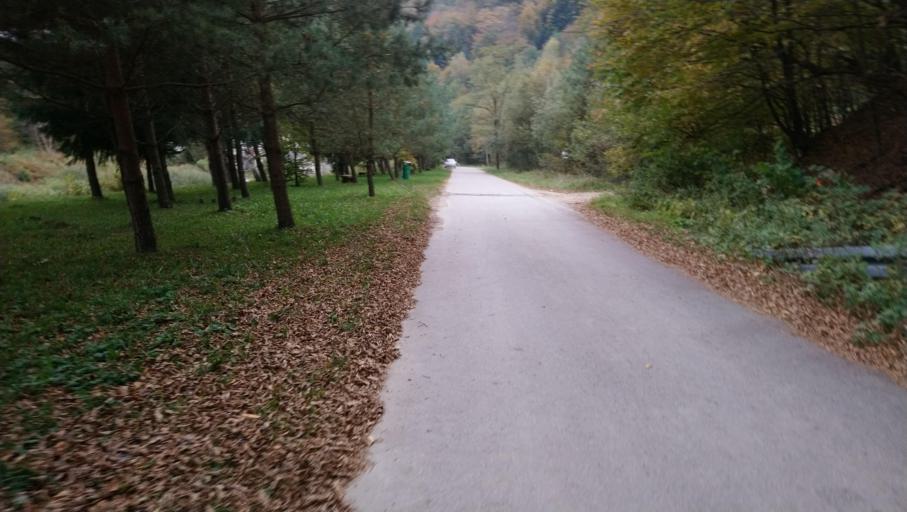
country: PL
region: Lesser Poland Voivodeship
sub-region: Powiat gorlicki
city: Ropa
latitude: 49.5614
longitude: 21.0857
